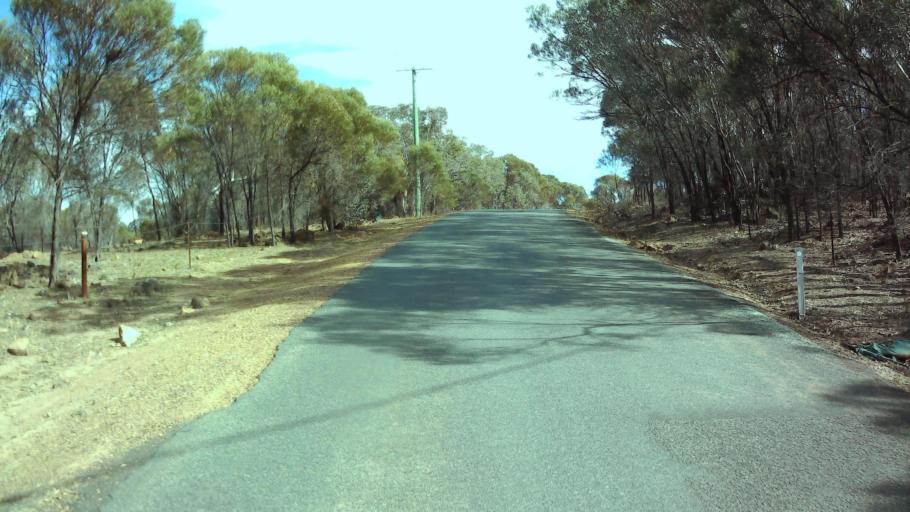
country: AU
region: New South Wales
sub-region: Weddin
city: Grenfell
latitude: -33.8784
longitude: 148.1927
